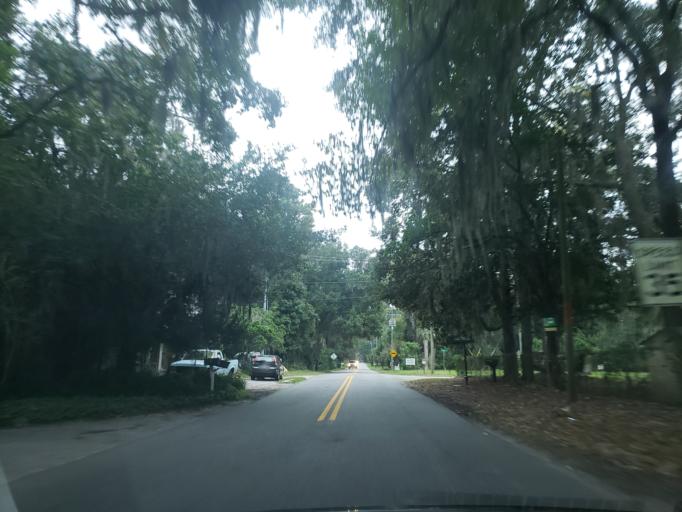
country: US
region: Georgia
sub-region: Chatham County
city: Montgomery
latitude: 31.9454
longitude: -81.1133
